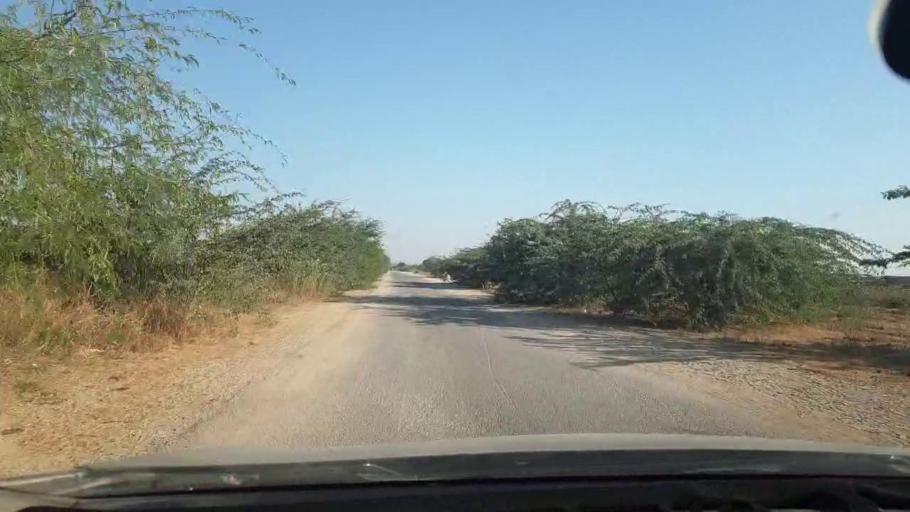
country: PK
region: Sindh
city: Malir Cantonment
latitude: 25.1703
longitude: 67.2007
